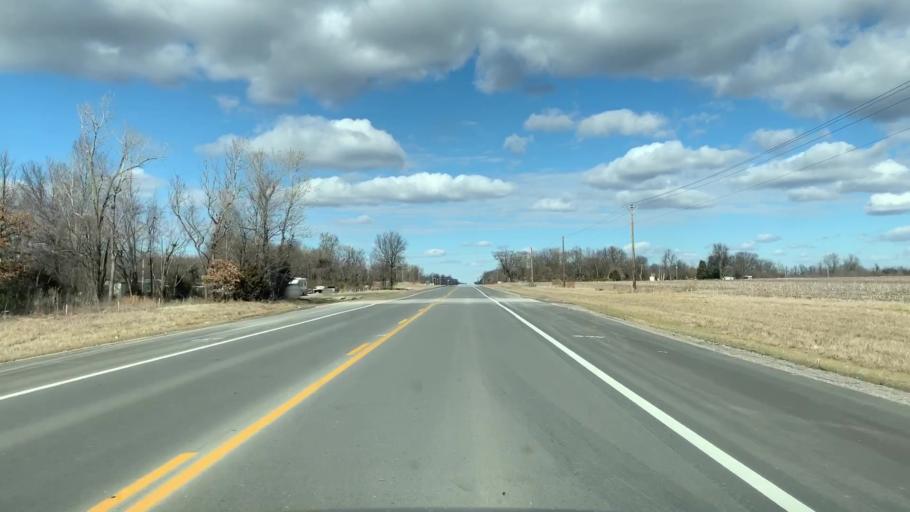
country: US
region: Kansas
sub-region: Cherokee County
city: Columbus
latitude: 37.2186
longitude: -94.8318
